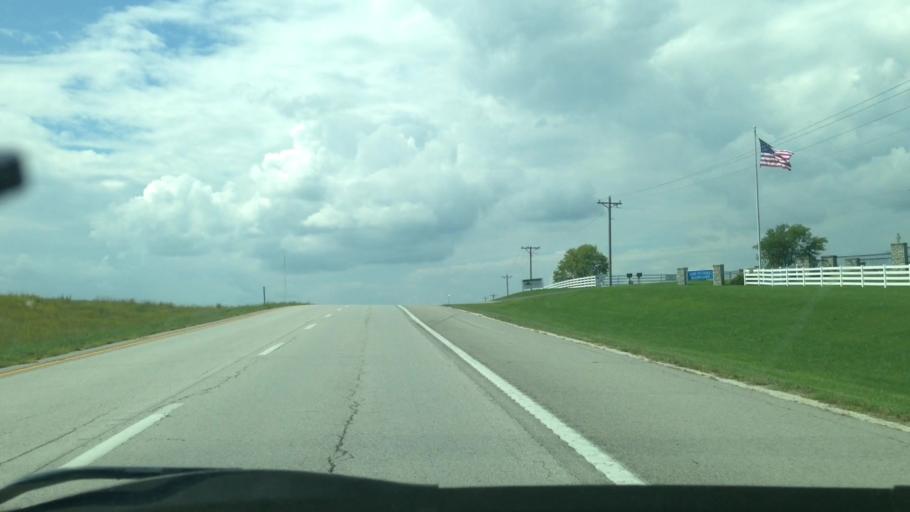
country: US
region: Missouri
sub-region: Pike County
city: Bowling Green
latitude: 39.2554
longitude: -91.0487
